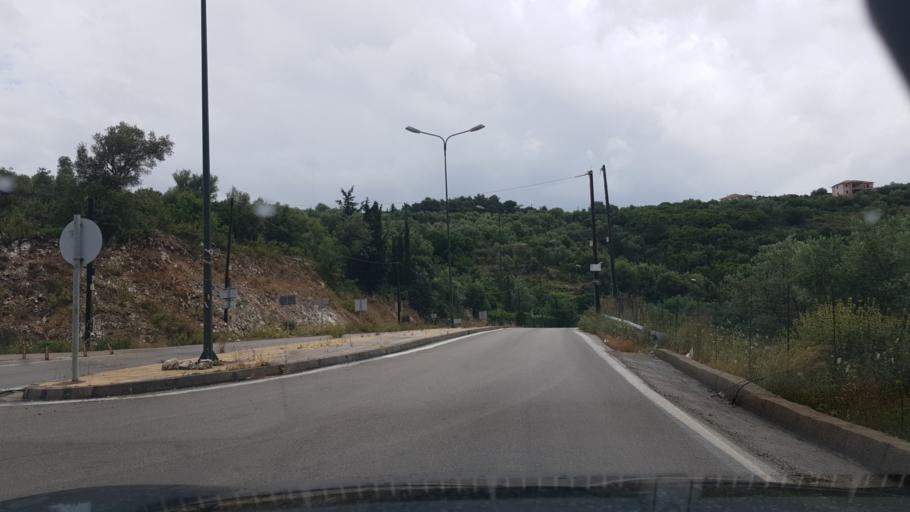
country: GR
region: Ionian Islands
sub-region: Lefkada
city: Nidri
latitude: 38.6507
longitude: 20.6803
